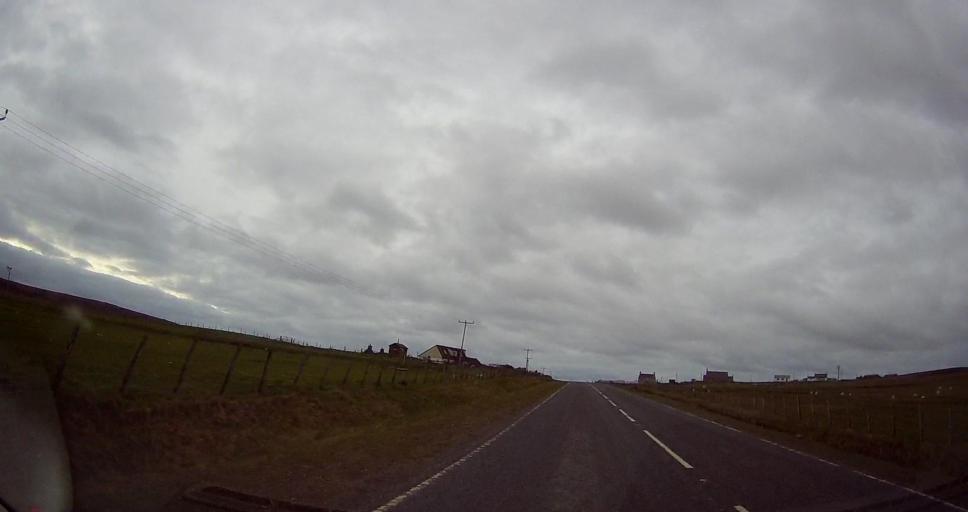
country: GB
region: Scotland
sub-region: Shetland Islands
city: Shetland
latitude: 60.6626
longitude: -1.0525
